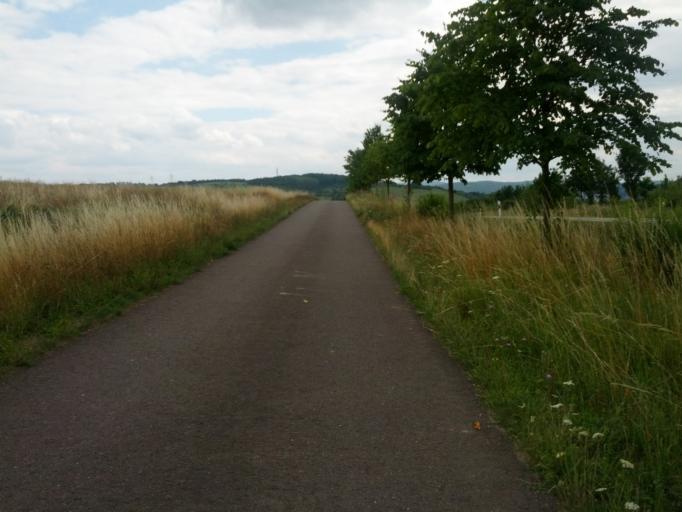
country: DE
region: Thuringia
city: Eisenach
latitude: 51.0068
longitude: 10.3186
